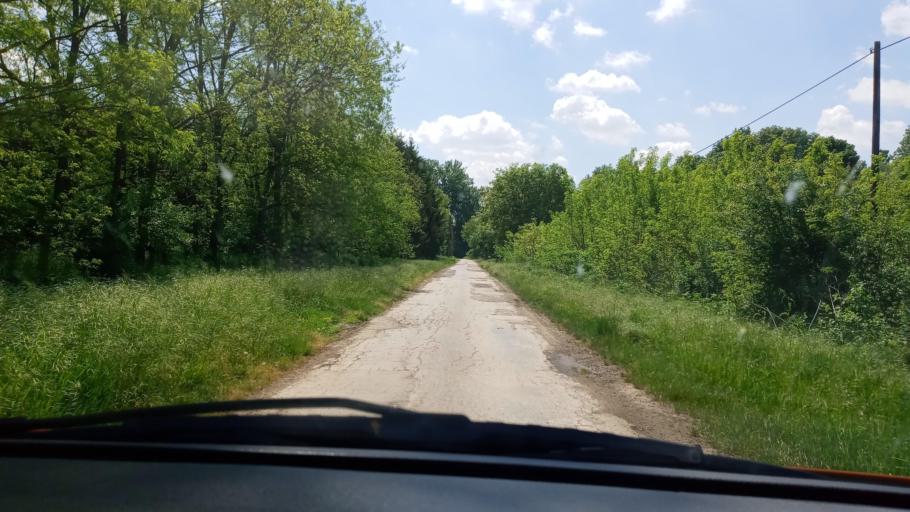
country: HU
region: Baranya
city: Siklos
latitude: 45.7735
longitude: 18.2753
